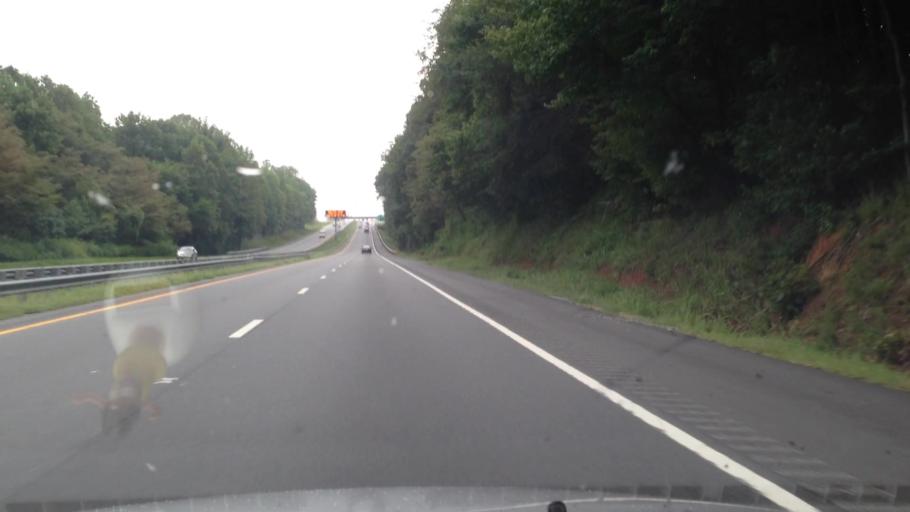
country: US
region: North Carolina
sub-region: Forsyth County
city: Kernersville
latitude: 36.1039
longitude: -80.0329
